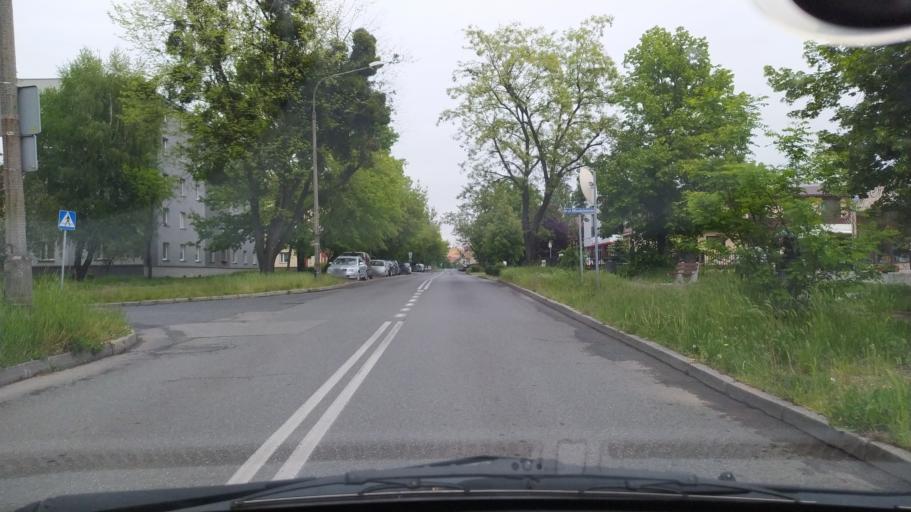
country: PL
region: Silesian Voivodeship
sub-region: Powiat gliwicki
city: Przyszowice
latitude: 50.2870
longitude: 18.7299
